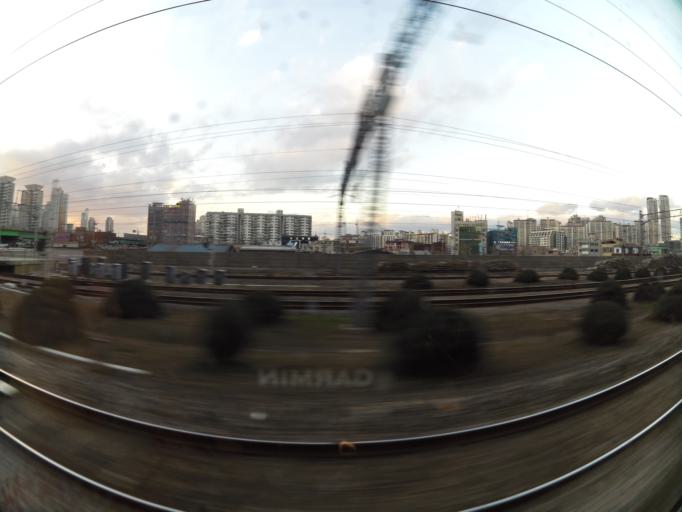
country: KR
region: Gyeonggi-do
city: Kwangmyong
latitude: 37.5100
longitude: 126.8941
